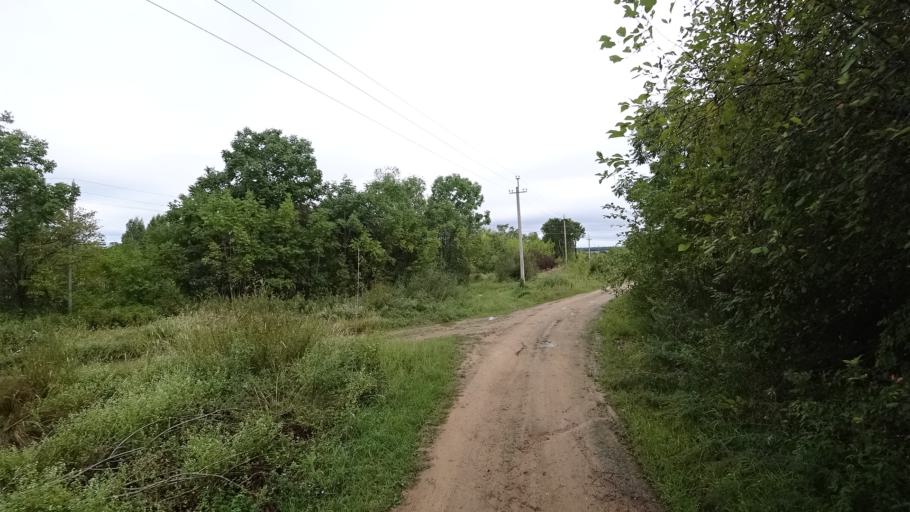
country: RU
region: Primorskiy
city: Rettikhovka
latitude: 44.1353
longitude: 132.6334
